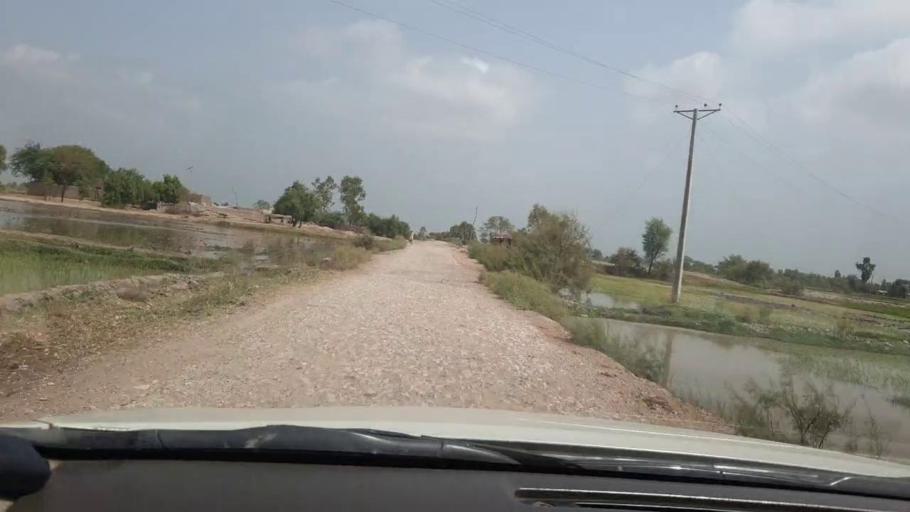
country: PK
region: Sindh
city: Garhi Yasin
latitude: 28.0149
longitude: 68.5285
